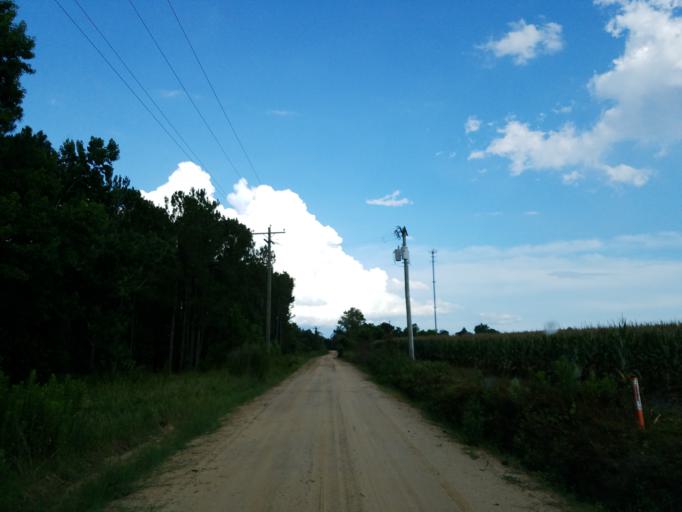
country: US
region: Georgia
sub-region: Turner County
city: Ashburn
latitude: 31.7451
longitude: -83.6629
